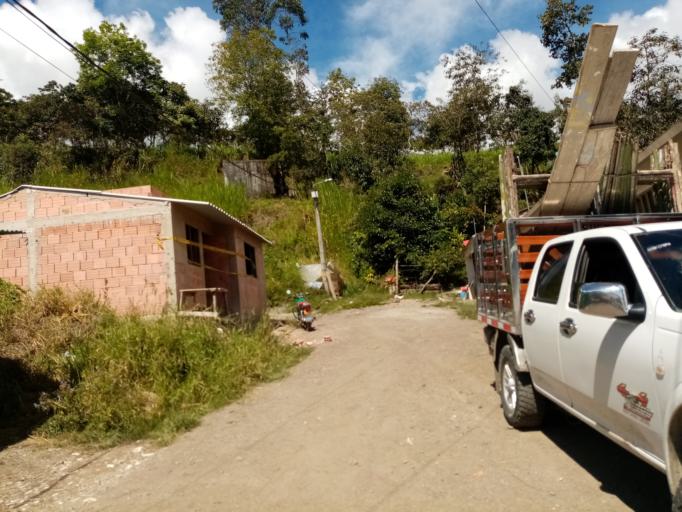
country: CO
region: Cundinamarca
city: Tenza
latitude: 5.0944
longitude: -73.4467
